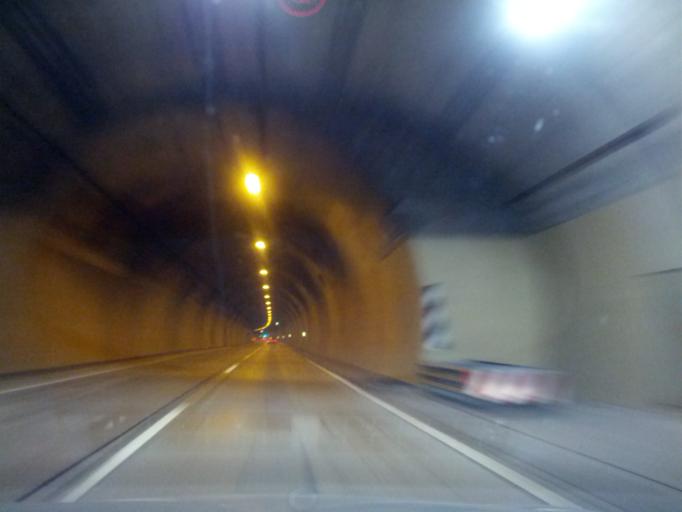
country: SI
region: Koper-Capodistria
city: Dekani
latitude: 45.5522
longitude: 13.8229
